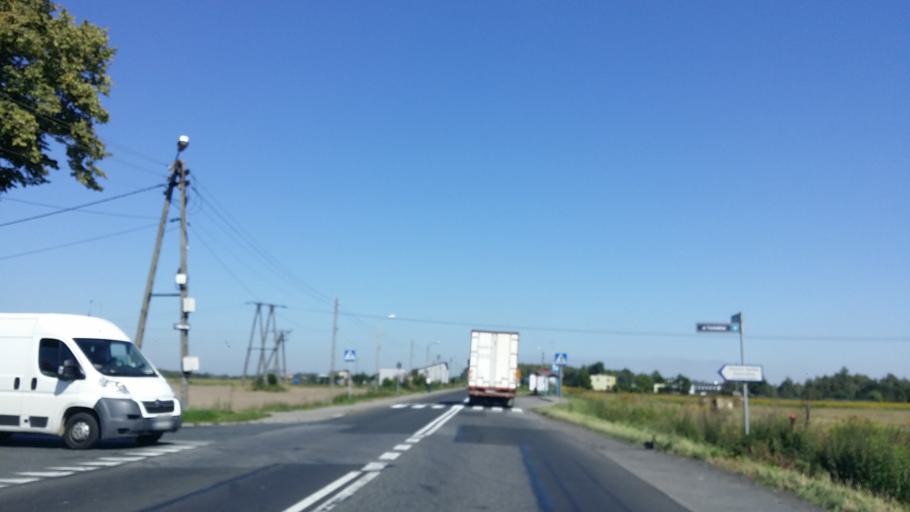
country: PL
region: Silesian Voivodeship
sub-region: Powiat bierunsko-ledzinski
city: Chelm Slaski
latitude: 50.1168
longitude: 19.2007
